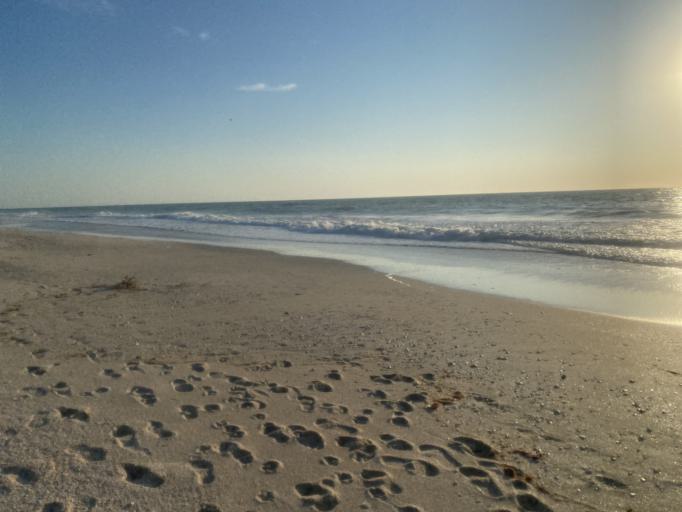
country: US
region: Florida
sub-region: Sarasota County
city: Laurel
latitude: 27.1387
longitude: -82.4758
